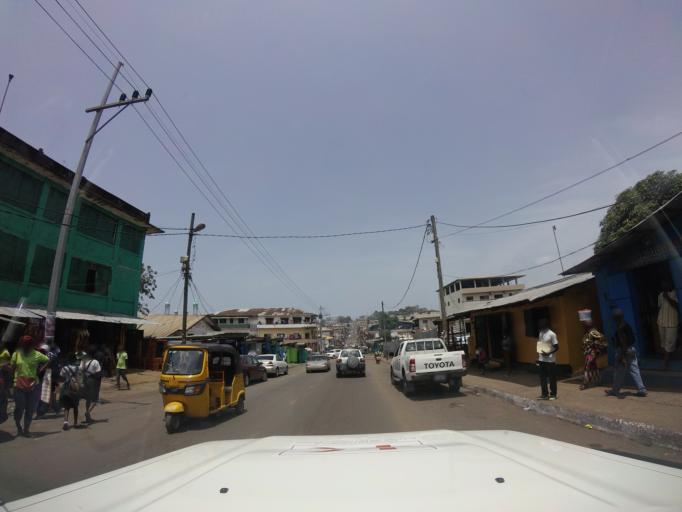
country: LR
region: Montserrado
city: Monrovia
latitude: 6.3140
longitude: -10.8028
